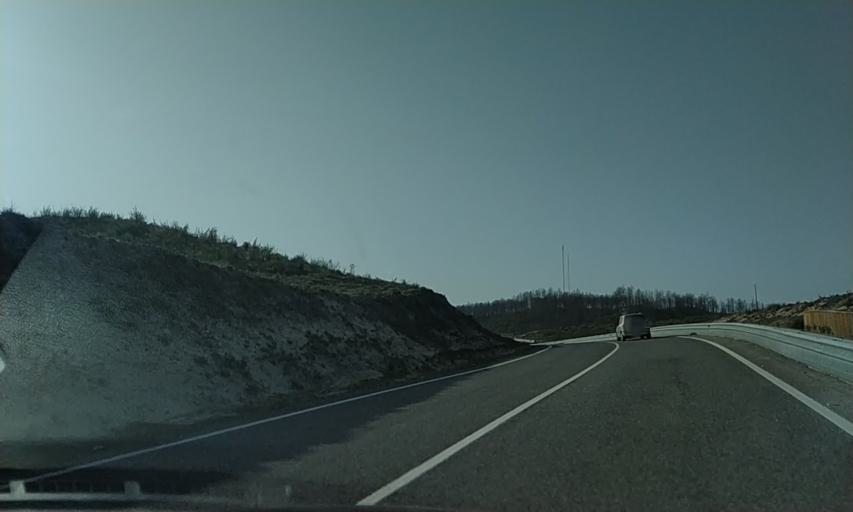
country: PT
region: Leiria
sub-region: Marinha Grande
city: Marinha Grande
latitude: 39.7447
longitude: -8.9841
